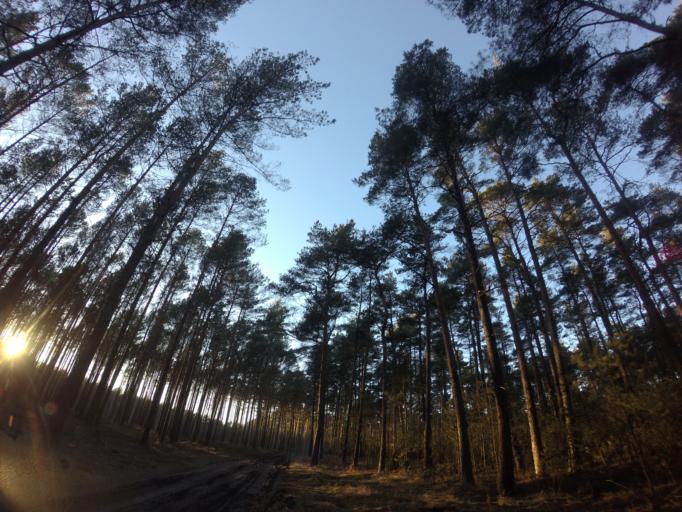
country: PL
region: West Pomeranian Voivodeship
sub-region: Powiat choszczenski
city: Drawno
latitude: 53.1179
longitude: 15.7542
